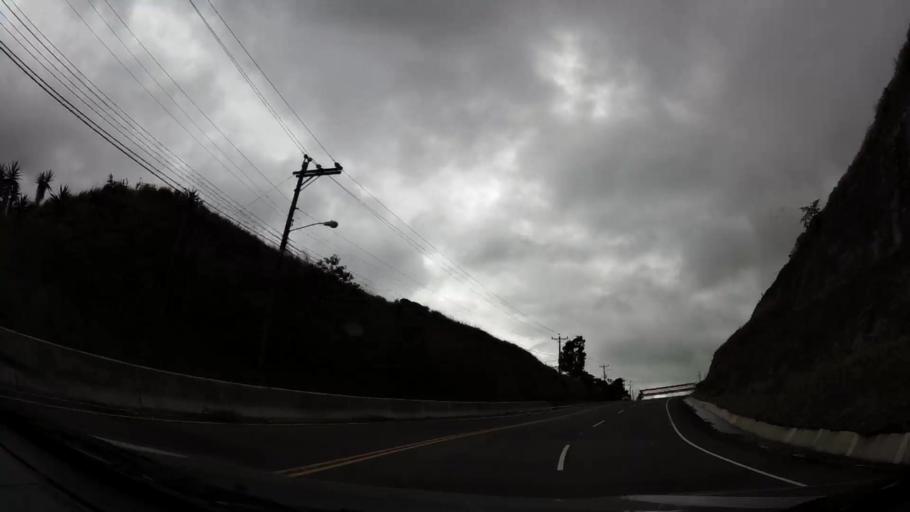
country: PA
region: Chiriqui
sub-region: Distrito Boquete
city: Boquete
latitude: 8.7590
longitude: -82.4326
